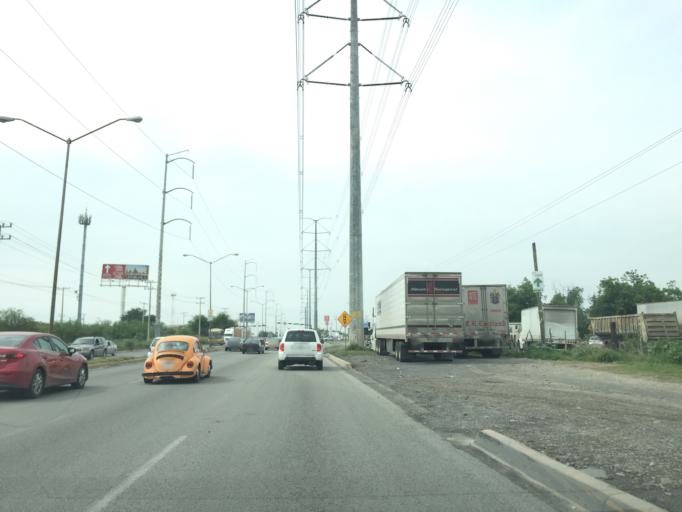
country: MX
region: Nuevo Leon
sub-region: Apodaca
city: Fraccionamiento Cosmopolis Octavo Sector
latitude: 25.7993
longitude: -100.2238
